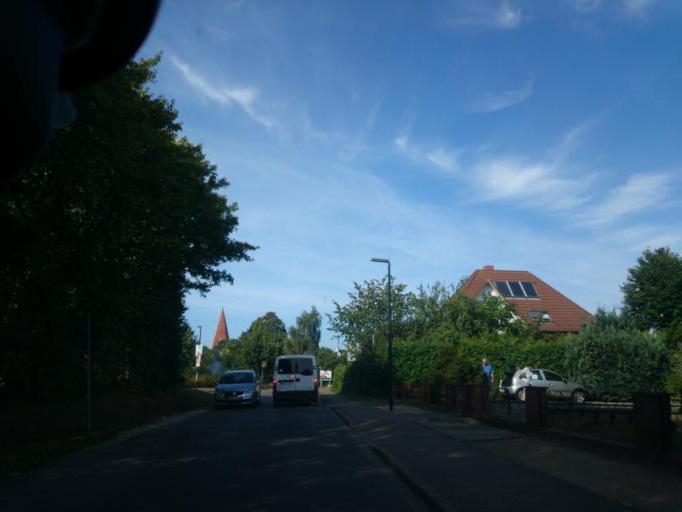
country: DE
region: Mecklenburg-Vorpommern
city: Elmenhorst
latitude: 54.1379
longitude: 12.0320
